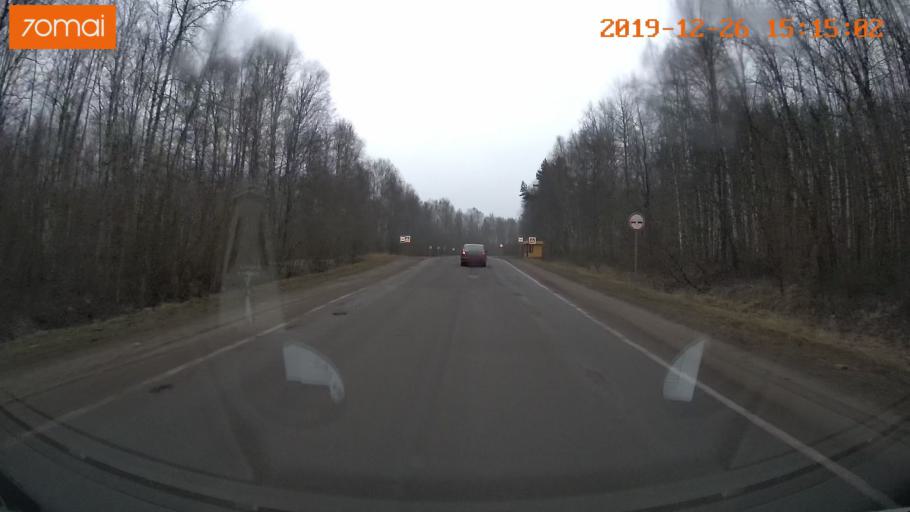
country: RU
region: Jaroslavl
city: Rybinsk
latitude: 58.1006
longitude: 38.8767
